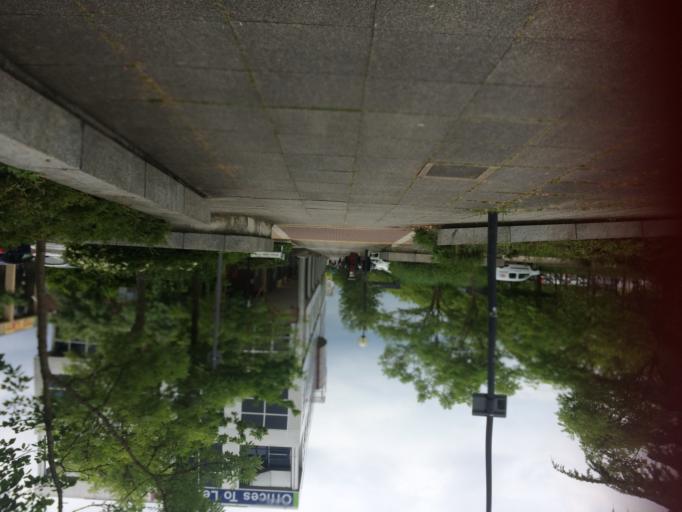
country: GB
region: England
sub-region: Milton Keynes
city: Milton Keynes
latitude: 52.0398
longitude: -0.7661
